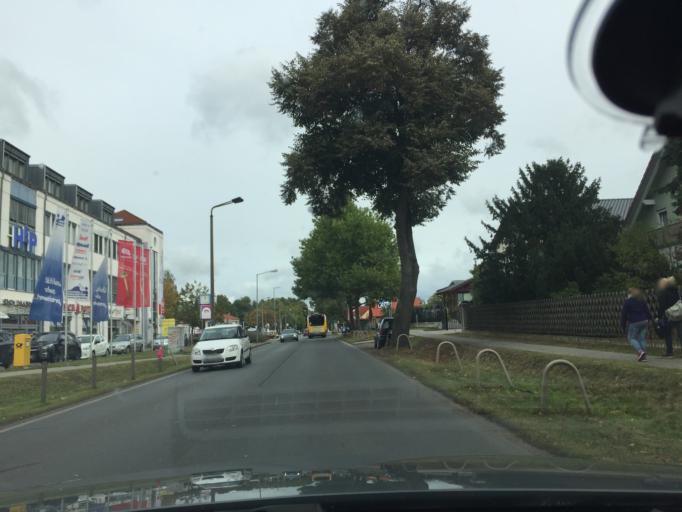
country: DE
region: Berlin
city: Hellersdorf
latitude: 52.5366
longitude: 13.6334
